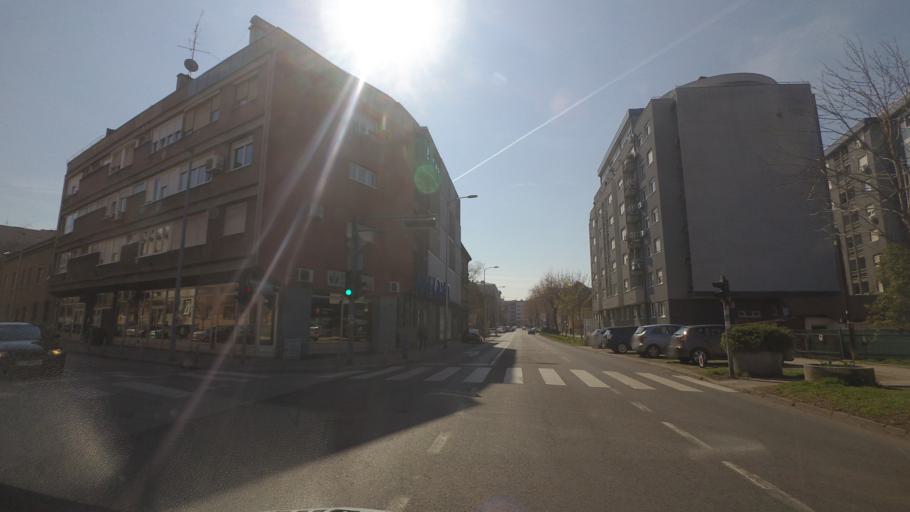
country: HR
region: Grad Zagreb
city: Zagreb - Centar
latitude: 45.8057
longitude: 15.9582
